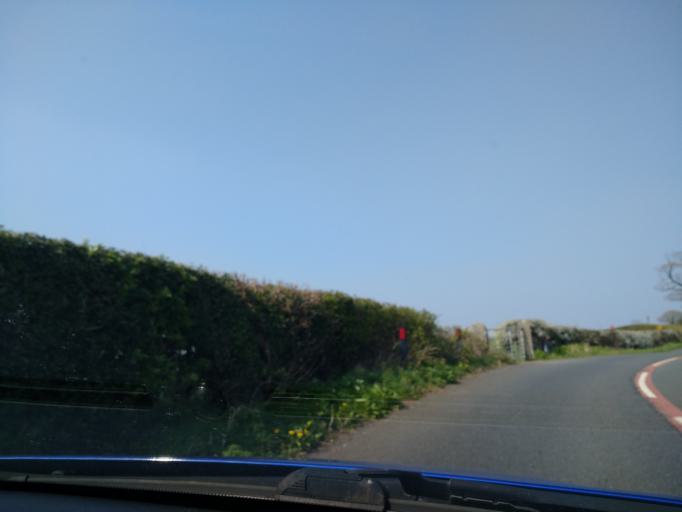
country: GB
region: England
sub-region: Lancashire
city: Bolton le Sands
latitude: 54.0829
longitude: -2.7867
